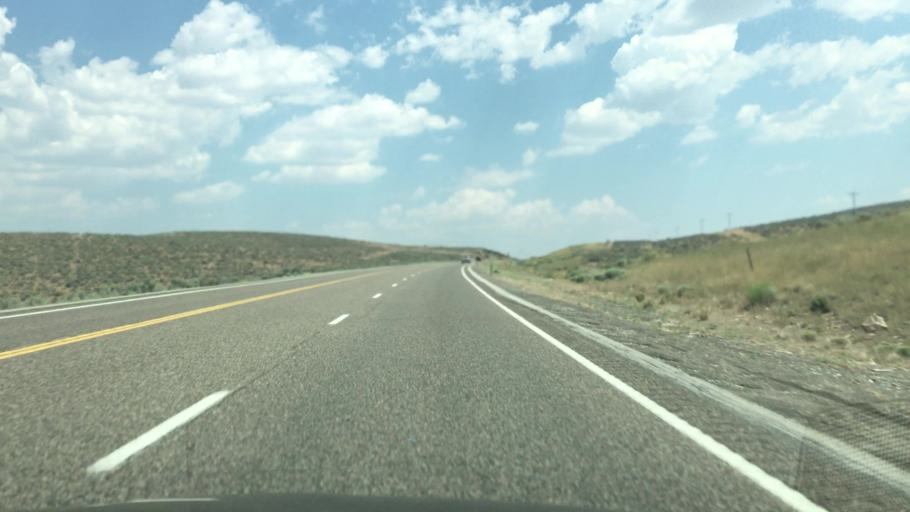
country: US
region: Nevada
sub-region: Elko County
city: Wells
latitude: 41.1865
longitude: -114.8737
